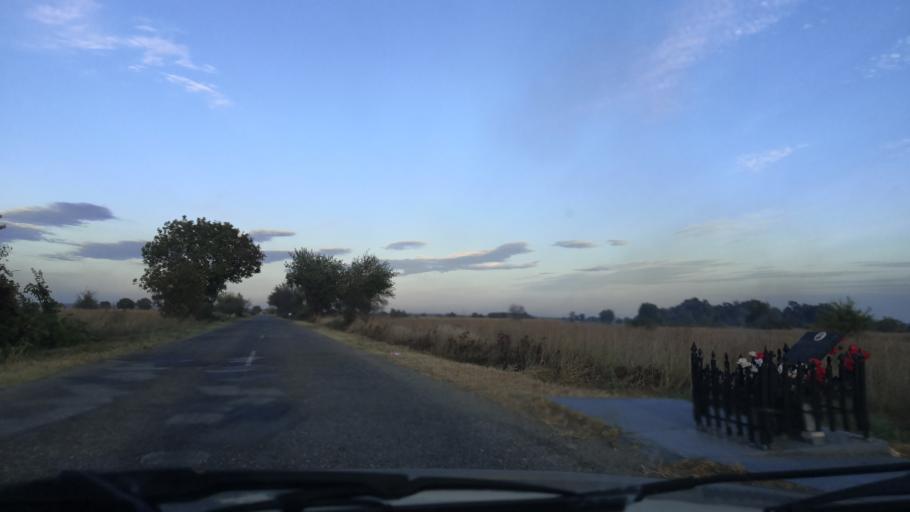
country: RS
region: Central Serbia
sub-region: Borski Okrug
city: Negotin
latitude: 44.2515
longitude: 22.6021
